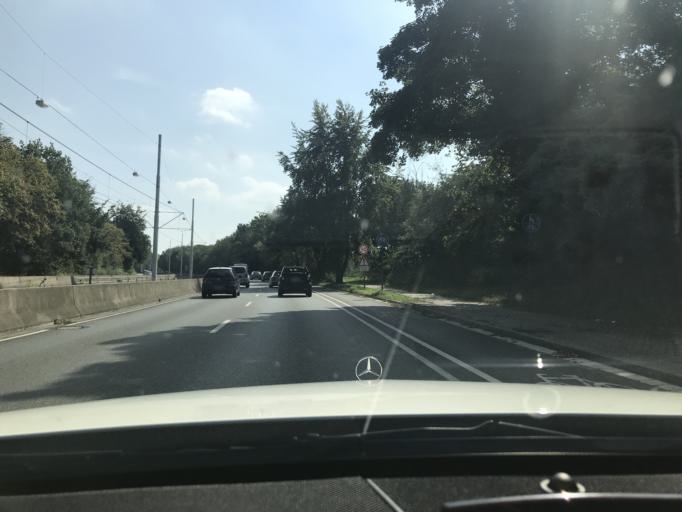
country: DE
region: North Rhine-Westphalia
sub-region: Regierungsbezirk Arnsberg
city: Bochum
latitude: 51.4567
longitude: 7.2391
